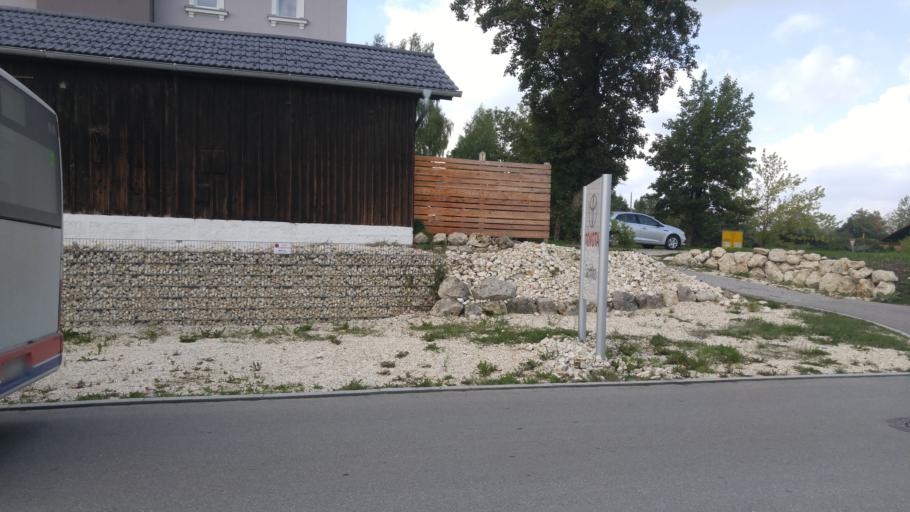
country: DE
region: Bavaria
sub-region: Swabia
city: Buchloe
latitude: 48.0367
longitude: 10.7199
